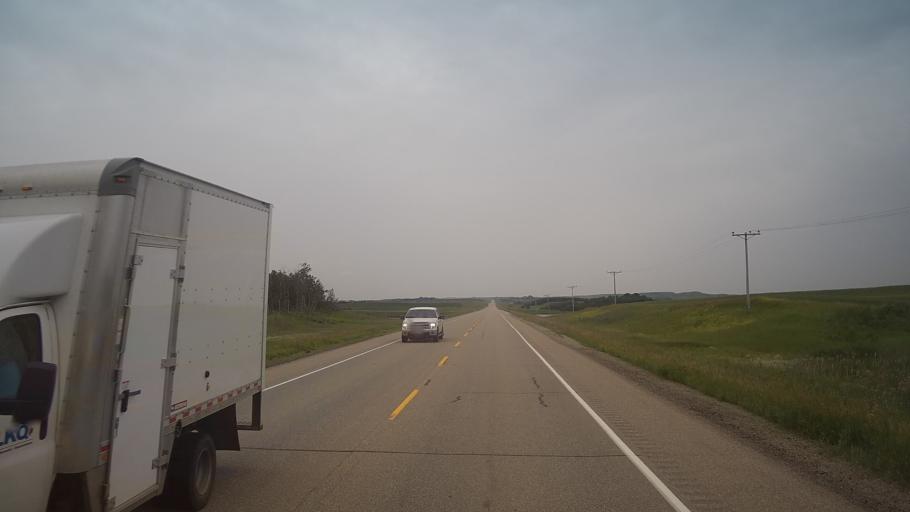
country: CA
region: Saskatchewan
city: Biggar
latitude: 52.0565
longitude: -107.8064
